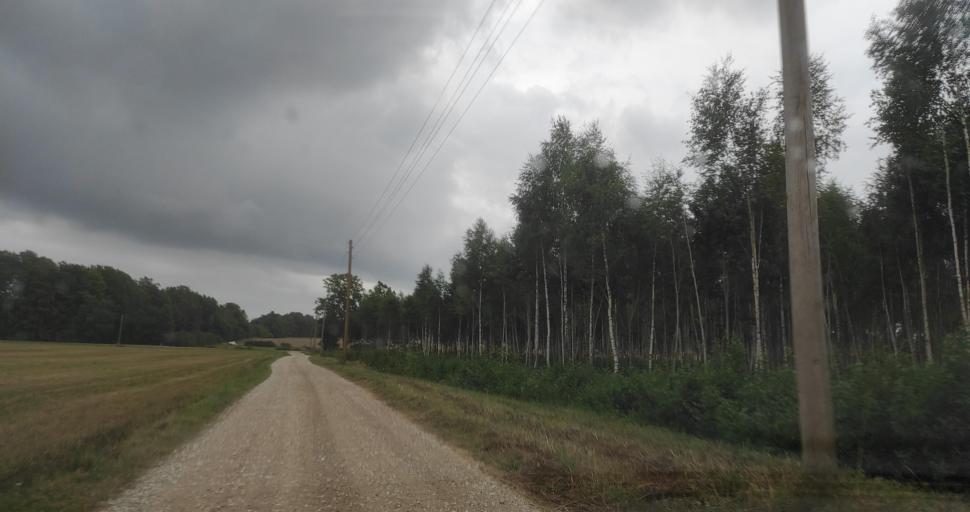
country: LV
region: Durbe
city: Liegi
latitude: 56.7033
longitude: 21.3627
